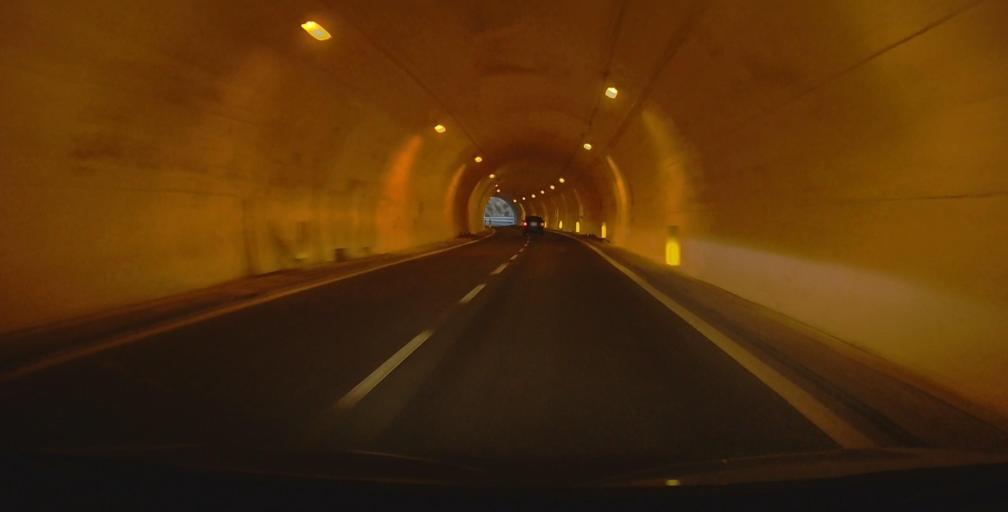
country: IT
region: Sicily
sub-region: Messina
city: Ali Terme
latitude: 38.0156
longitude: 15.4330
